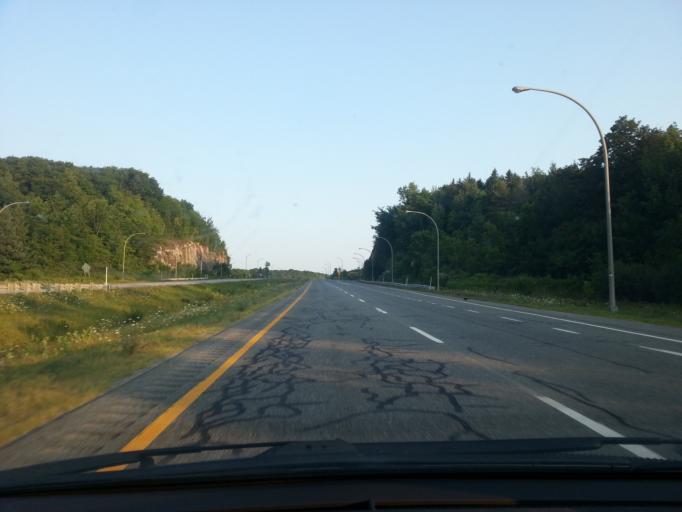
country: CA
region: Quebec
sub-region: Outaouais
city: Gatineau
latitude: 45.5119
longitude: -75.8037
